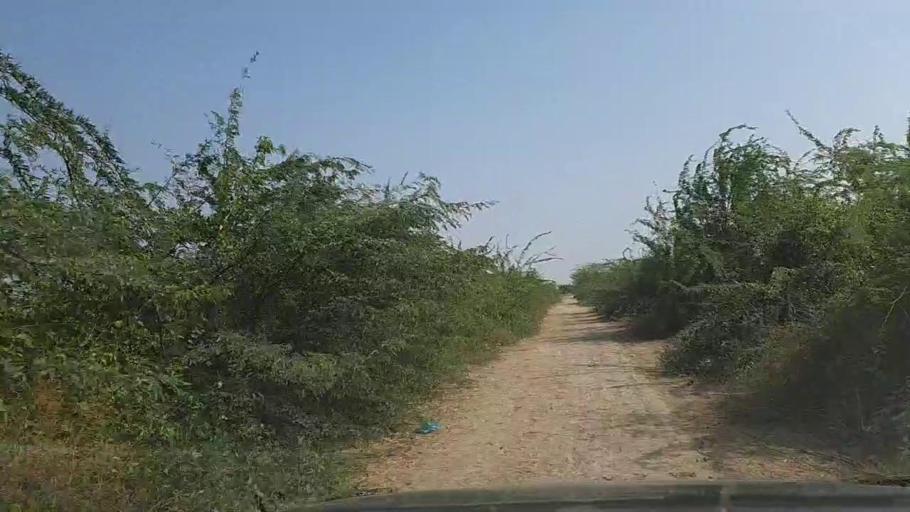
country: PK
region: Sindh
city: Gharo
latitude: 24.7388
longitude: 67.6852
